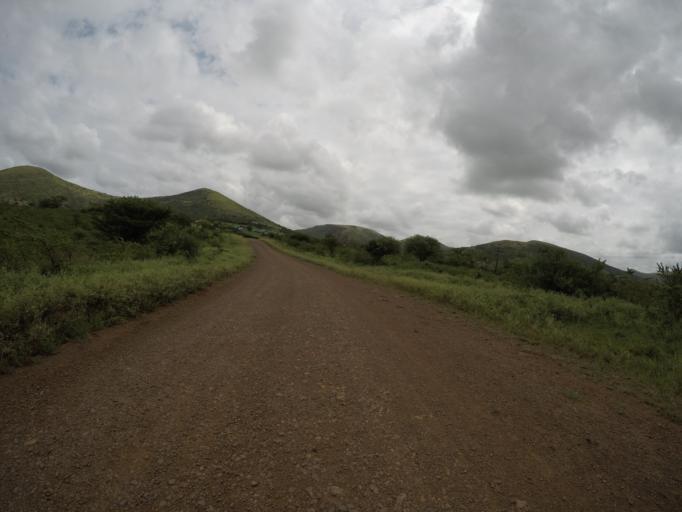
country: ZA
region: KwaZulu-Natal
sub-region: uThungulu District Municipality
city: Empangeni
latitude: -28.5926
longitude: 31.8908
